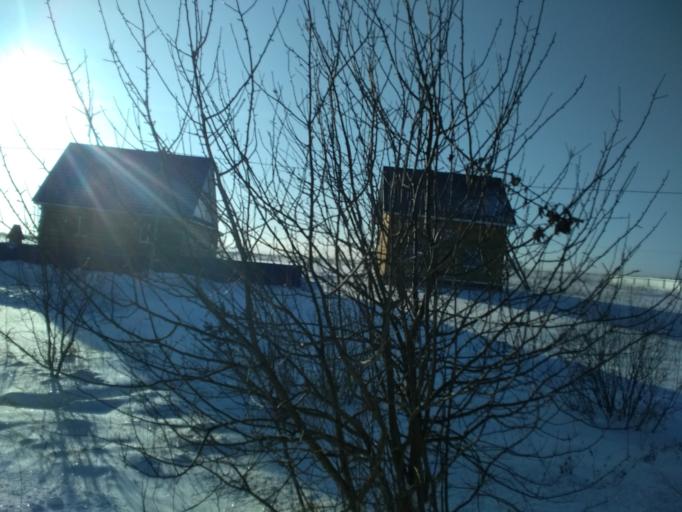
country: RU
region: Bashkortostan
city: Iglino
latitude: 54.6845
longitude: 56.6040
